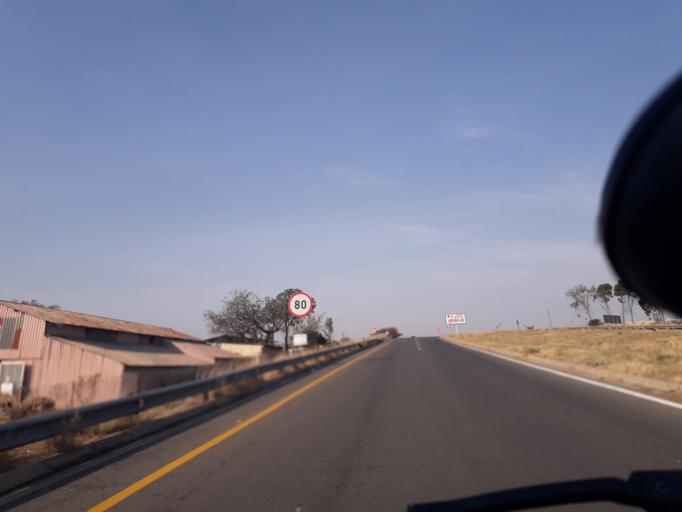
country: ZA
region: Gauteng
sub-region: City of Johannesburg Metropolitan Municipality
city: Diepsloot
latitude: -25.9689
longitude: 27.9197
